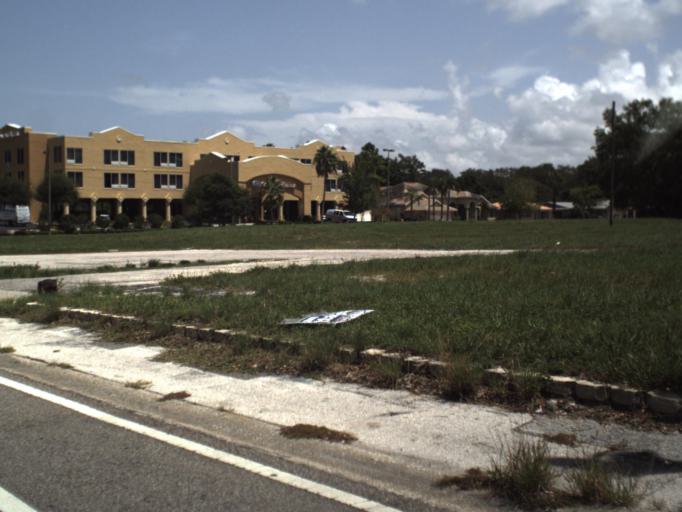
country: US
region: Florida
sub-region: Pinellas County
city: Clearwater
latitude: 27.9907
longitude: -82.7956
